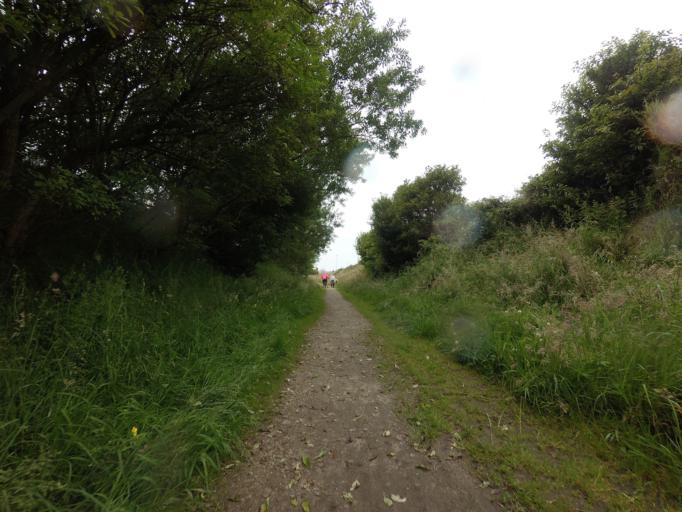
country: GB
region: Scotland
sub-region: Moray
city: Portknockie
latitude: 57.7011
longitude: -2.8545
